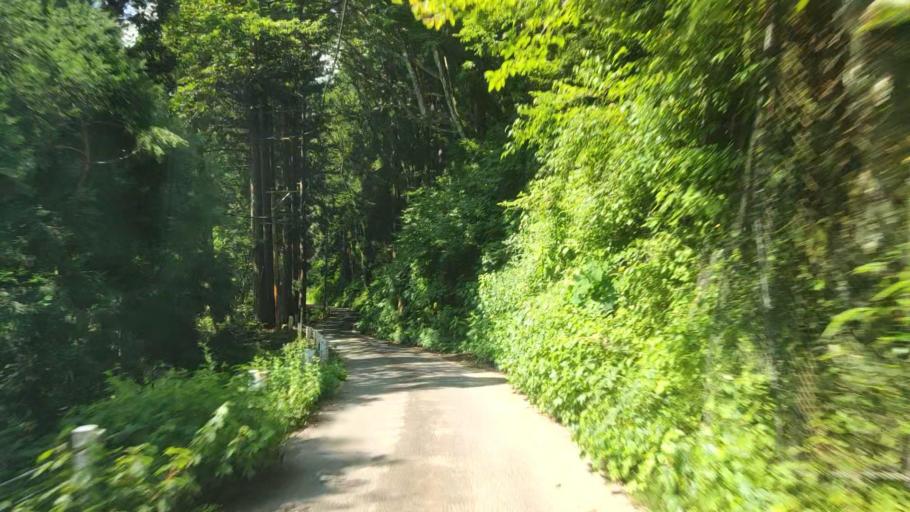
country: JP
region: Ishikawa
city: Komatsu
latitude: 36.2431
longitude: 136.5318
